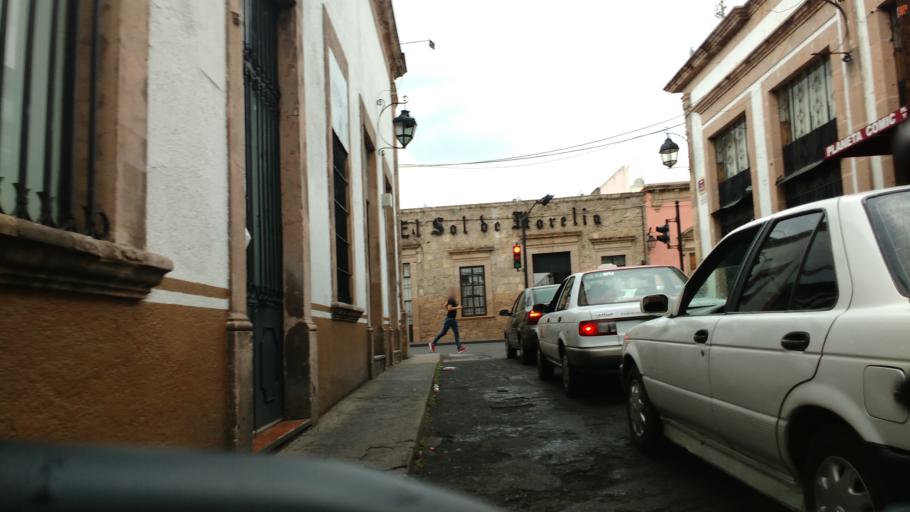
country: MX
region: Michoacan
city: Morelia
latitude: 19.7027
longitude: -101.1839
